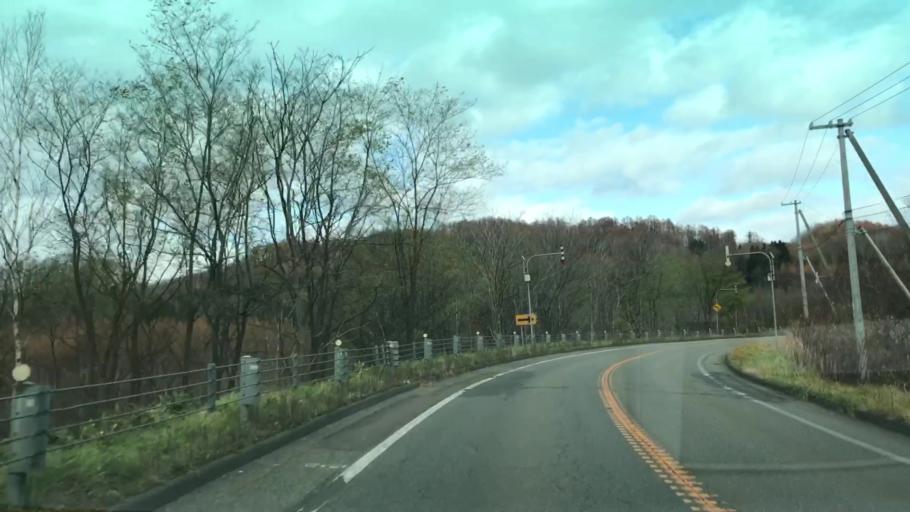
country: JP
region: Hokkaido
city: Shimo-furano
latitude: 42.8867
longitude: 142.4339
